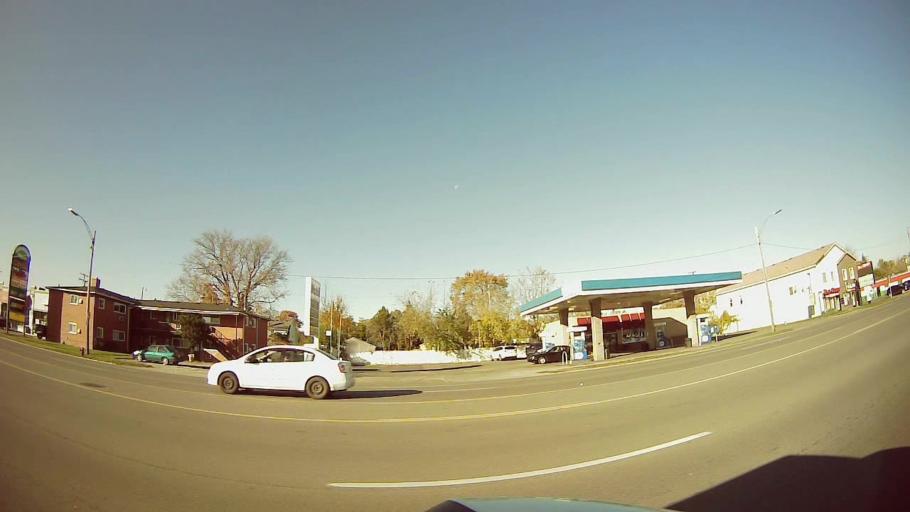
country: US
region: Michigan
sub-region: Wayne County
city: Dearborn
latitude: 42.3417
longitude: -83.1961
